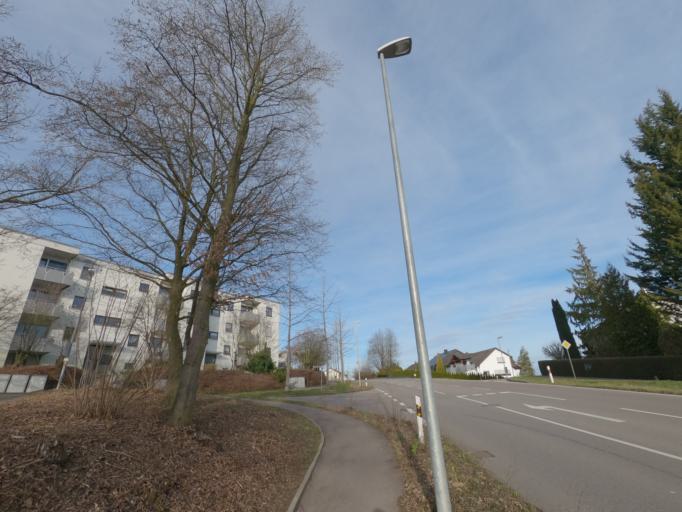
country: DE
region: Baden-Wuerttemberg
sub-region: Regierungsbezirk Stuttgart
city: Uhingen
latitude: 48.7015
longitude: 9.5824
